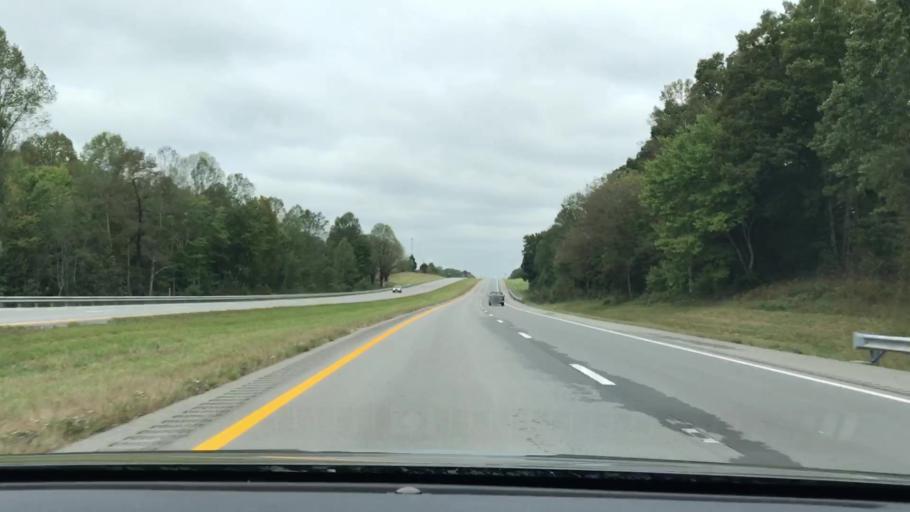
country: US
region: Kentucky
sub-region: Russell County
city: Russell Springs
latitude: 37.0480
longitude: -85.1464
